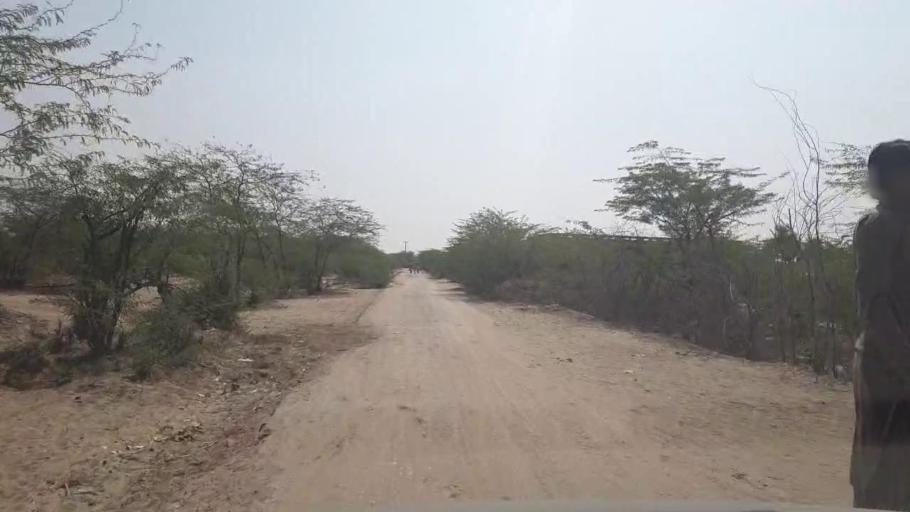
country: PK
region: Sindh
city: Chor
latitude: 25.4772
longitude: 69.7803
